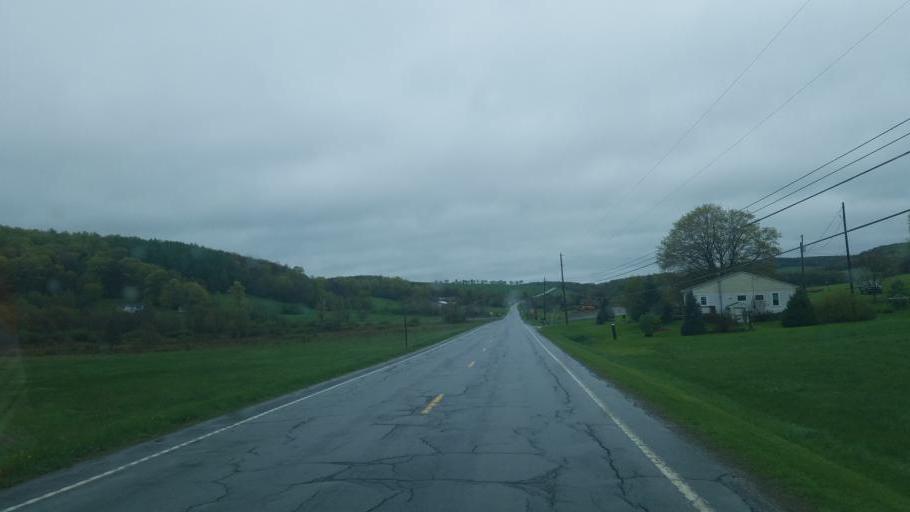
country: US
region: Pennsylvania
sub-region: Potter County
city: Galeton
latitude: 41.8942
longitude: -77.7866
